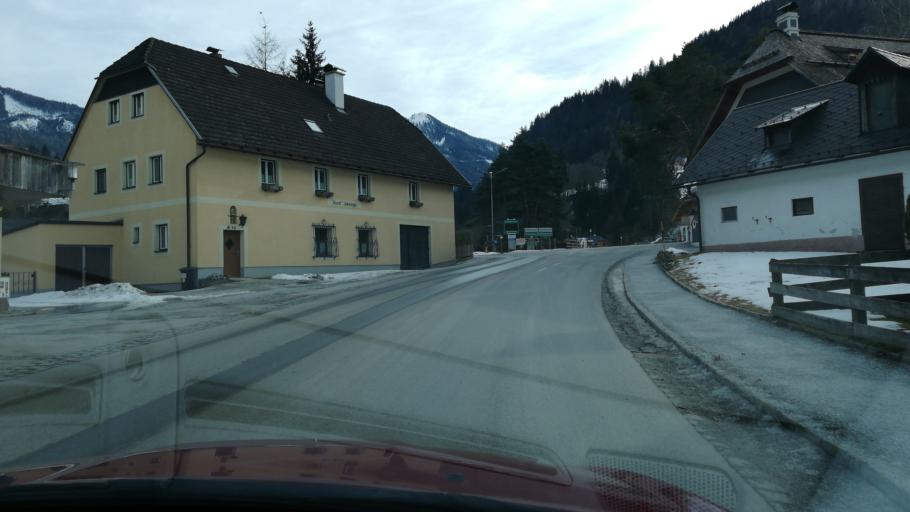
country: AT
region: Styria
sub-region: Politischer Bezirk Liezen
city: Donnersbach
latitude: 47.4645
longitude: 14.1295
